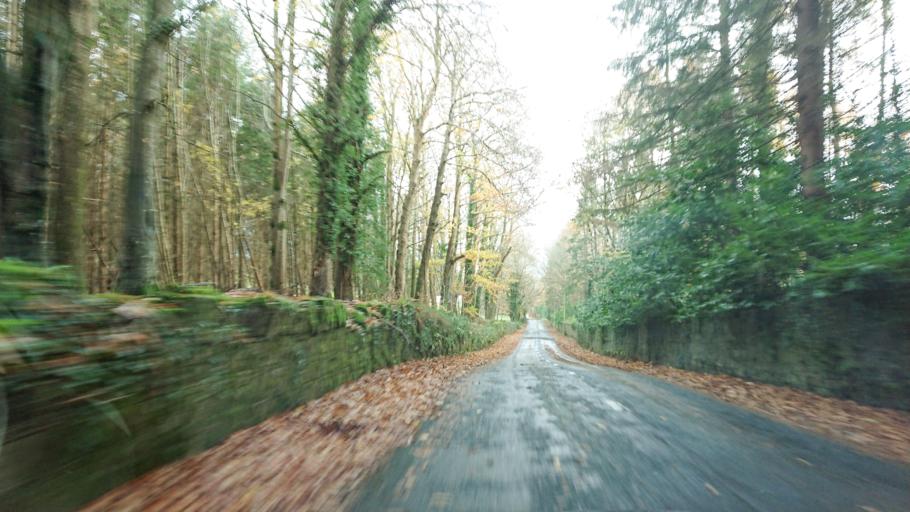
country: IE
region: Munster
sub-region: South Tipperary
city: Cluain Meala
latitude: 52.3569
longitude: -7.5930
